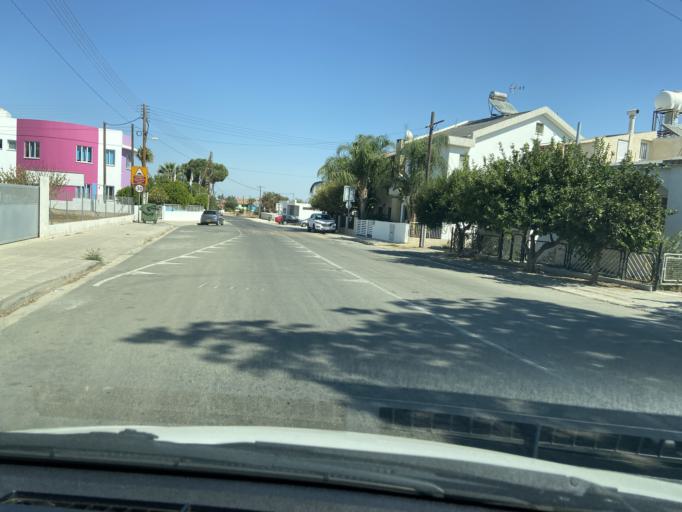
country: CY
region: Lefkosia
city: Kato Deftera
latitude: 35.0857
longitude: 33.2858
